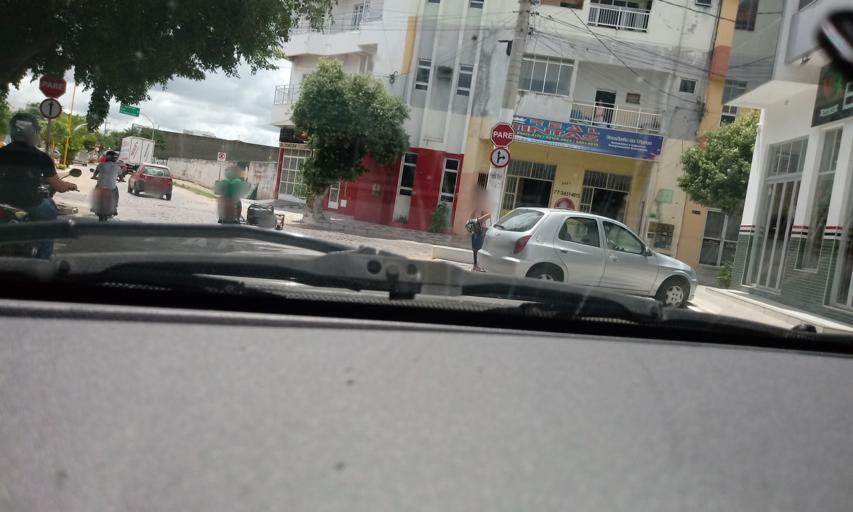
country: BR
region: Bahia
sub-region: Guanambi
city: Guanambi
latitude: -14.2246
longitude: -42.7761
